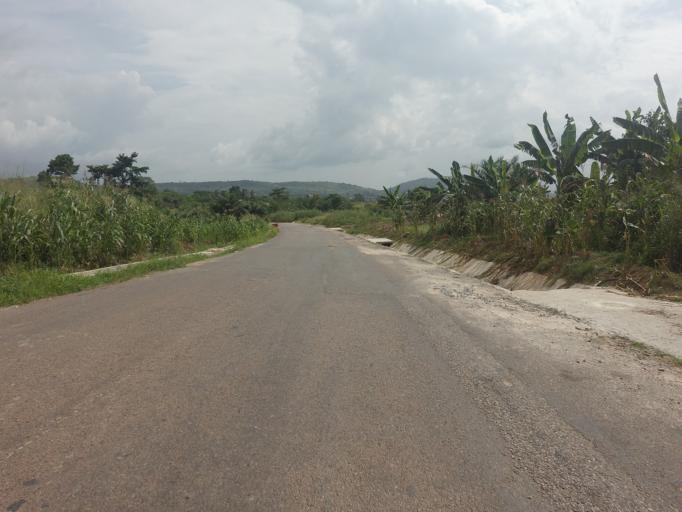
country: GH
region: Eastern
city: Aburi
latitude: 5.9607
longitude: -0.2176
